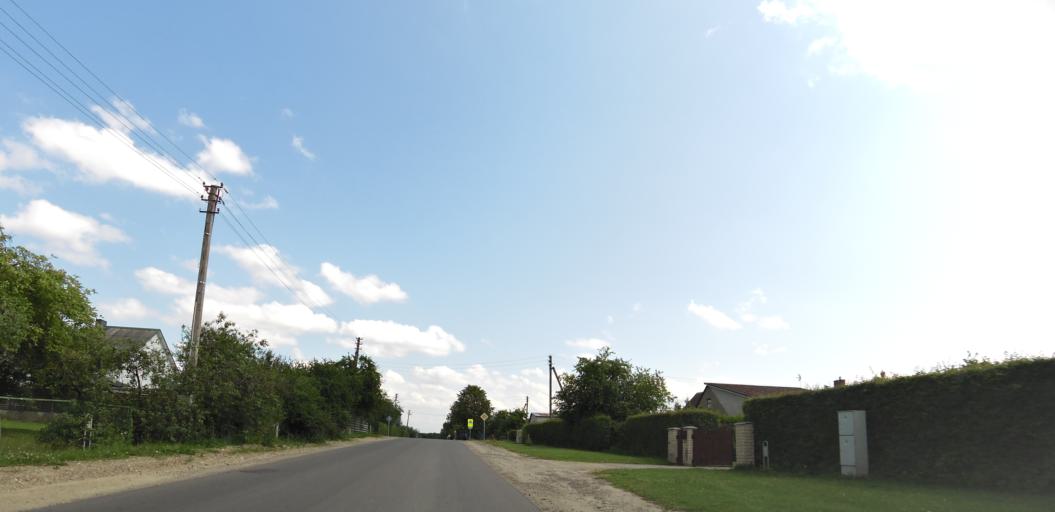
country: LT
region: Vilnius County
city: Pilaite
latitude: 54.7254
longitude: 25.1846
